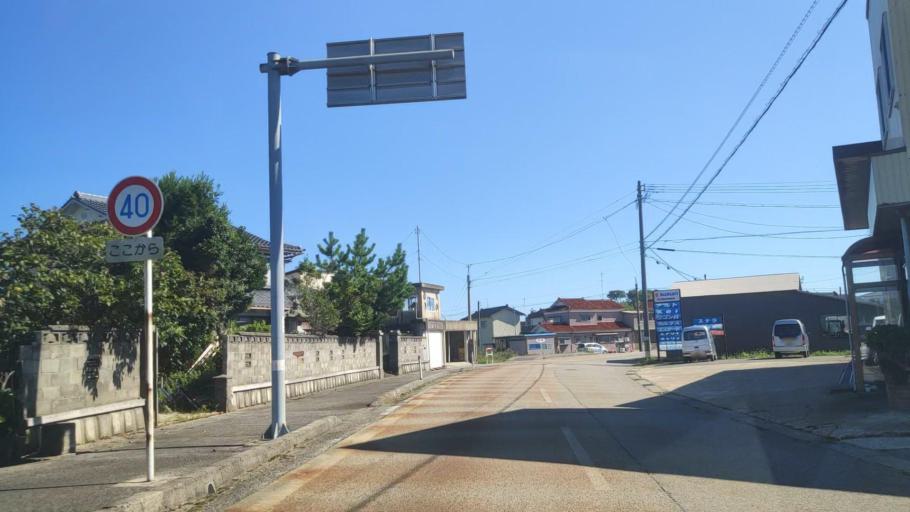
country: JP
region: Ishikawa
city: Nanao
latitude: 37.4496
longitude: 137.2896
